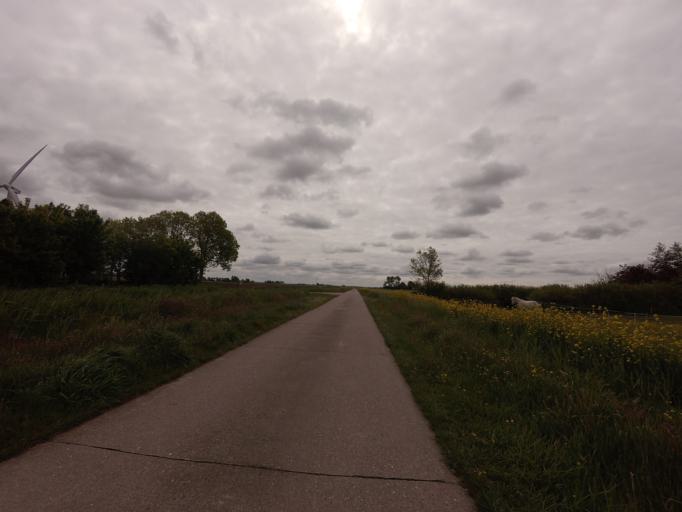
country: NL
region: Friesland
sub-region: Sudwest Fryslan
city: Workum
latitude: 52.9509
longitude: 5.4530
